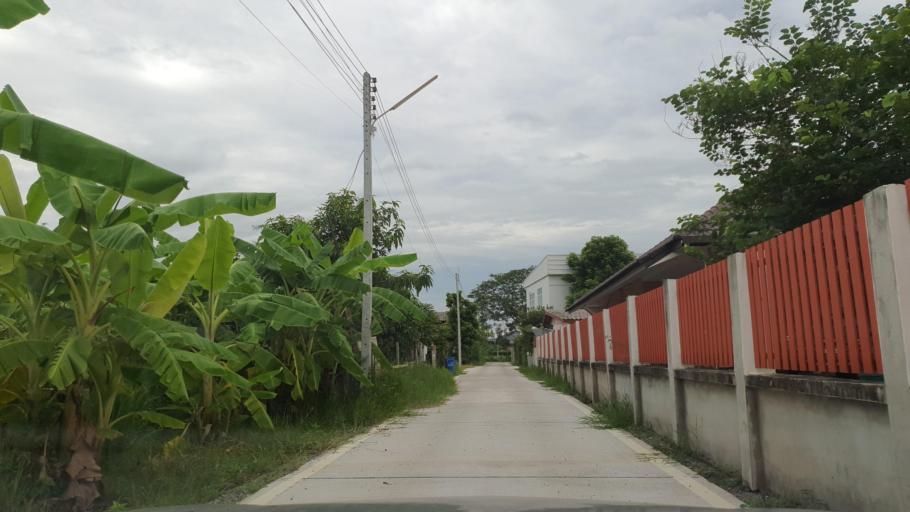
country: TH
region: Chiang Mai
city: Saraphi
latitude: 18.7518
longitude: 99.0692
